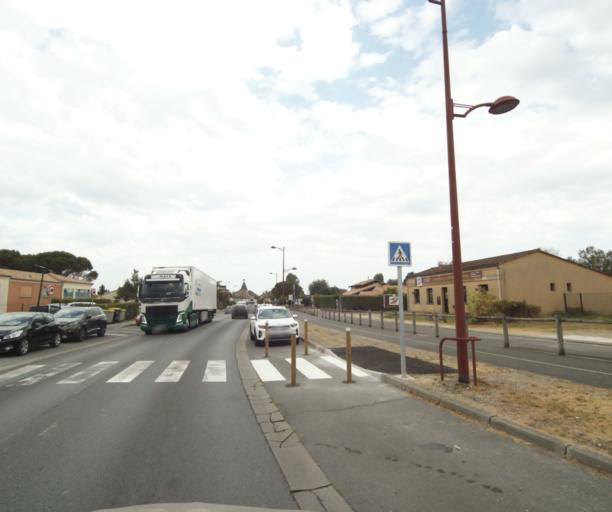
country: FR
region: Aquitaine
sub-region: Departement de la Gironde
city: Creon
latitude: 44.7722
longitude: -0.3446
